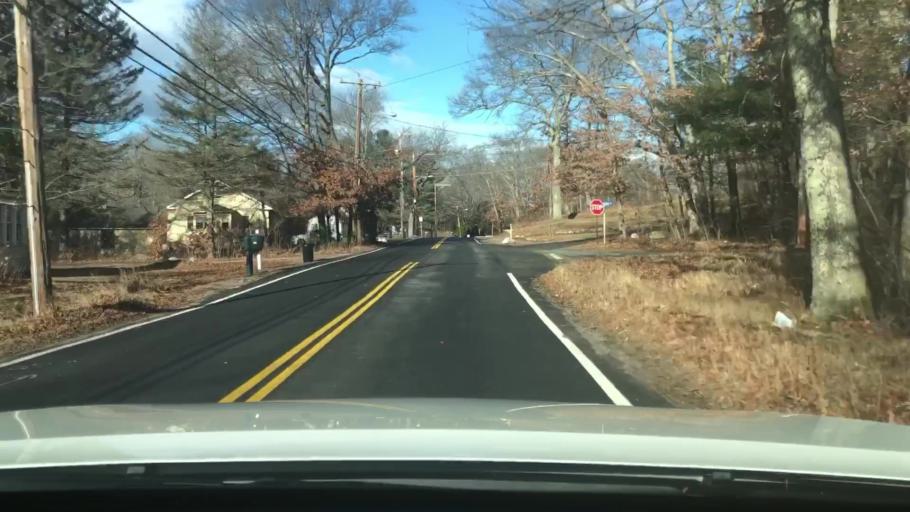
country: US
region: Massachusetts
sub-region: Worcester County
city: Blackstone
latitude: 42.0329
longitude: -71.5174
